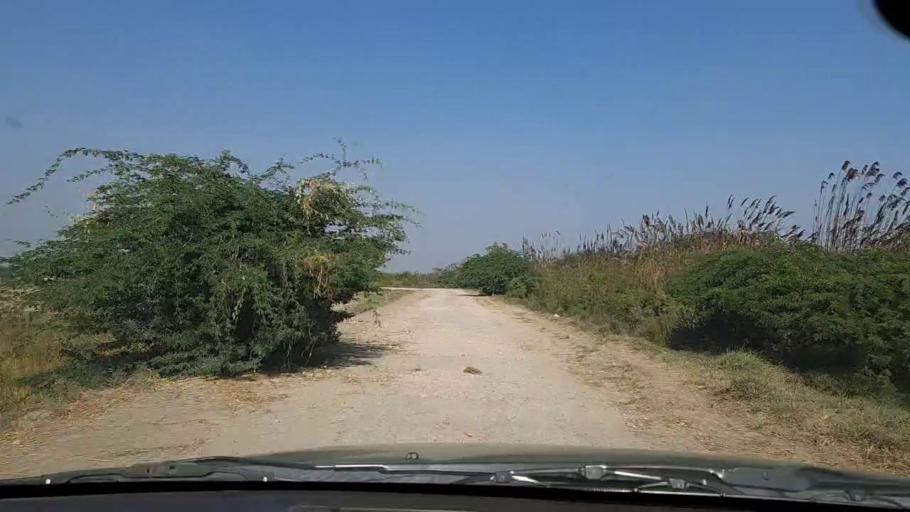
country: PK
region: Sindh
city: Chuhar Jamali
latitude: 24.4316
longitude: 67.7996
